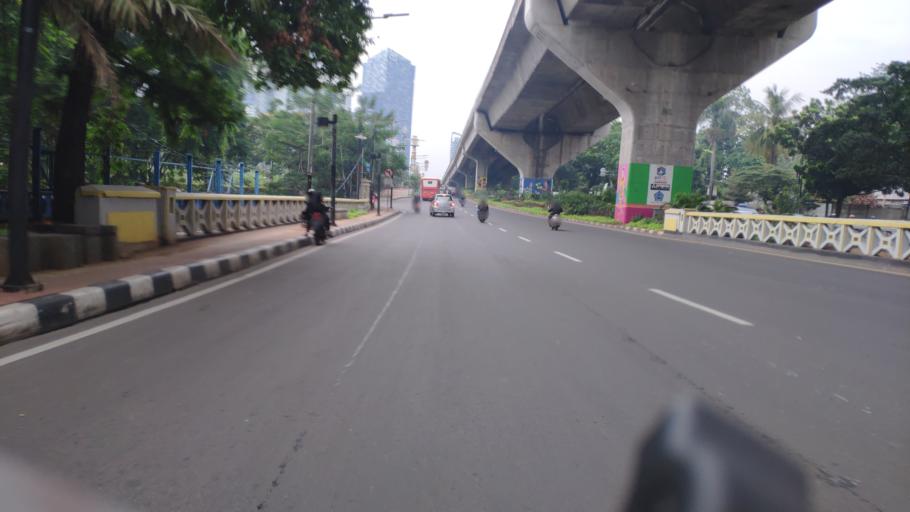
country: ID
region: Jakarta Raya
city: Jakarta
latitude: -6.2256
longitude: 106.8349
